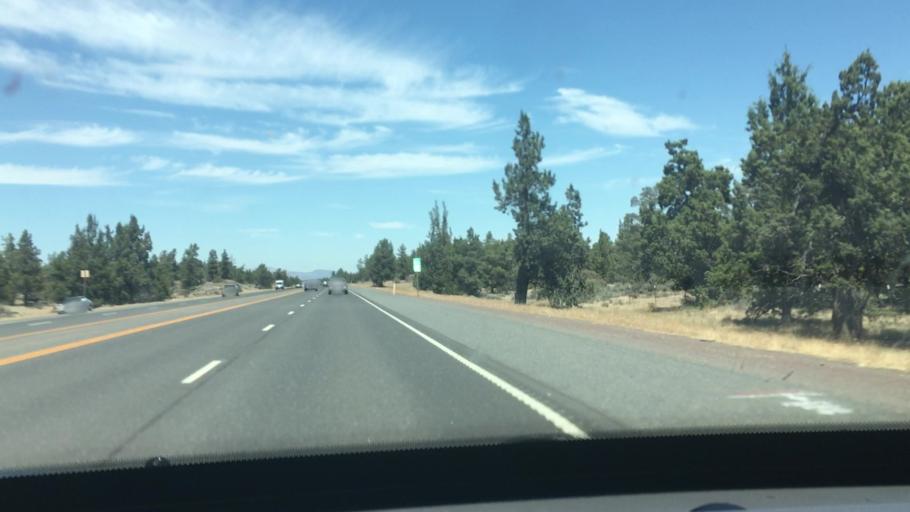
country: US
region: Oregon
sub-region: Deschutes County
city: Bend
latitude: 44.1379
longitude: -121.2745
